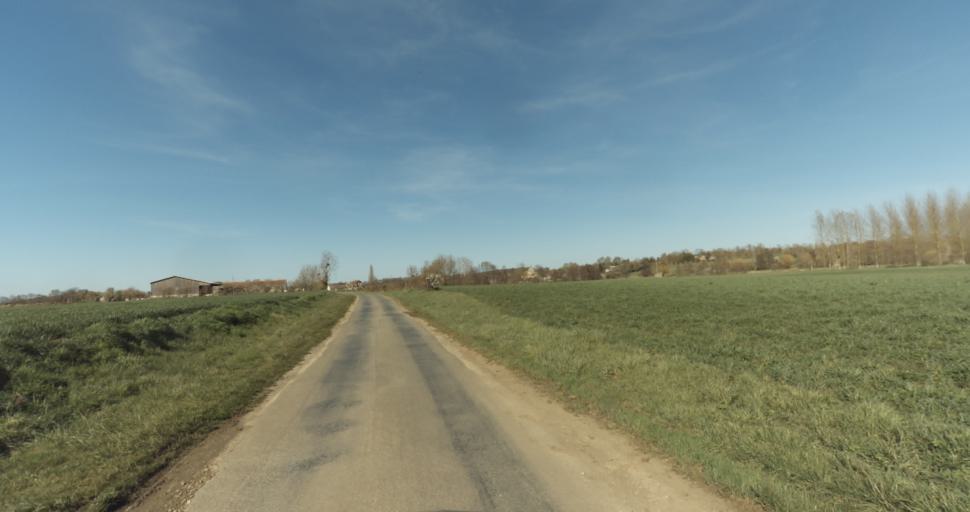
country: FR
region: Lower Normandy
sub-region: Departement du Calvados
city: Saint-Pierre-sur-Dives
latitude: 49.0471
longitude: -0.0266
